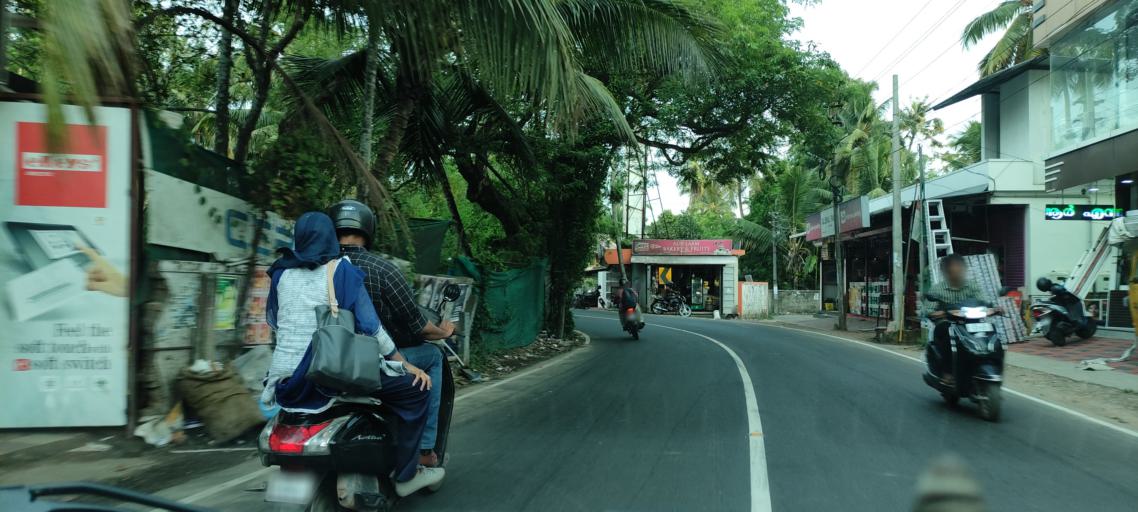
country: IN
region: Kerala
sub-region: Alappuzha
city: Arukutti
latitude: 9.8620
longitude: 76.3236
